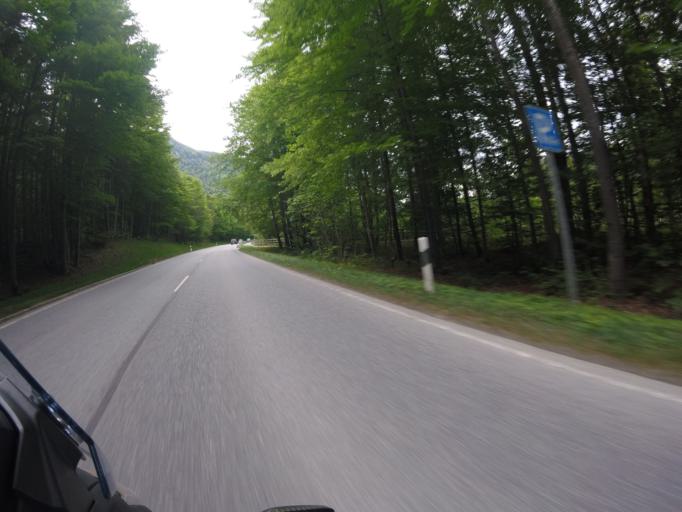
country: DE
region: Bavaria
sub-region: Upper Bavaria
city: Lenggries
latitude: 47.6238
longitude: 11.5956
